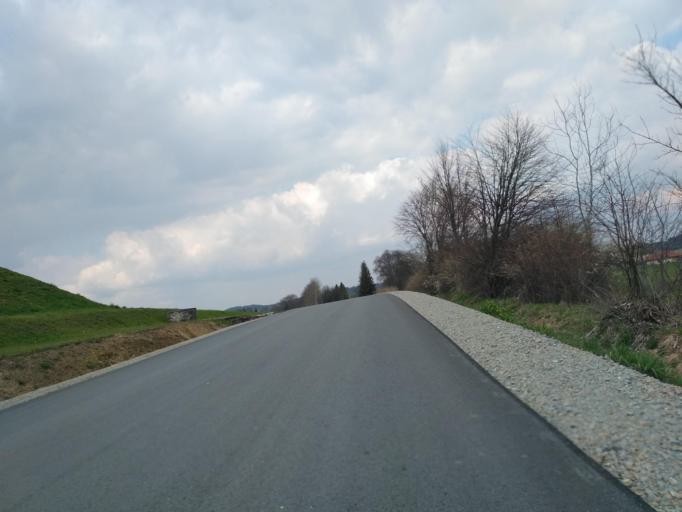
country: PL
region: Subcarpathian Voivodeship
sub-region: Powiat sanocki
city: Strachocina
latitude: 49.5967
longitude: 22.0984
